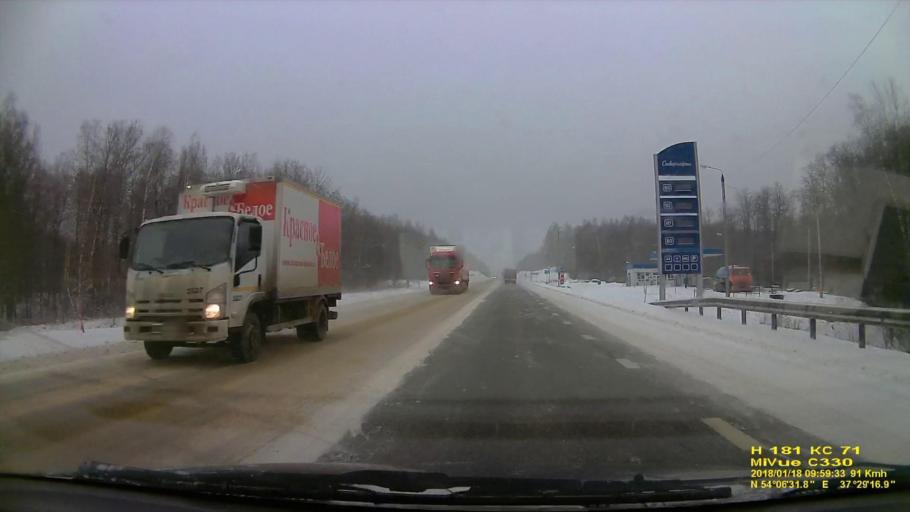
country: RU
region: Tula
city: Kosaya Gora
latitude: 54.1087
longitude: 37.4880
